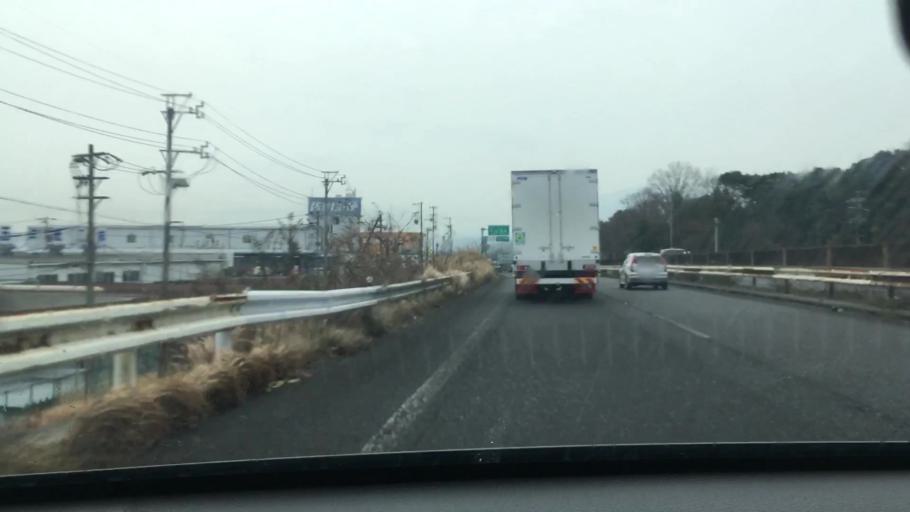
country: JP
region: Mie
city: Ueno-ebisumachi
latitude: 34.7976
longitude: 136.1773
